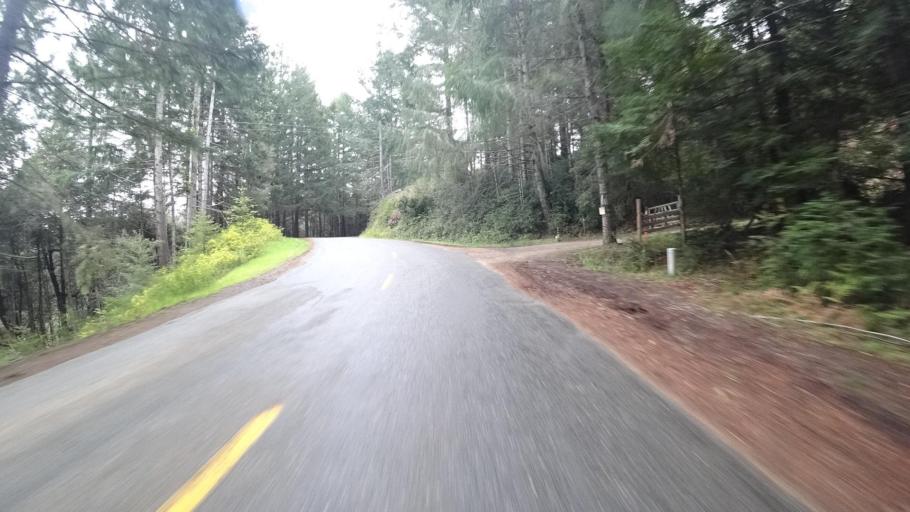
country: US
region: California
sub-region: Humboldt County
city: Redway
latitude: 40.2772
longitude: -123.7877
